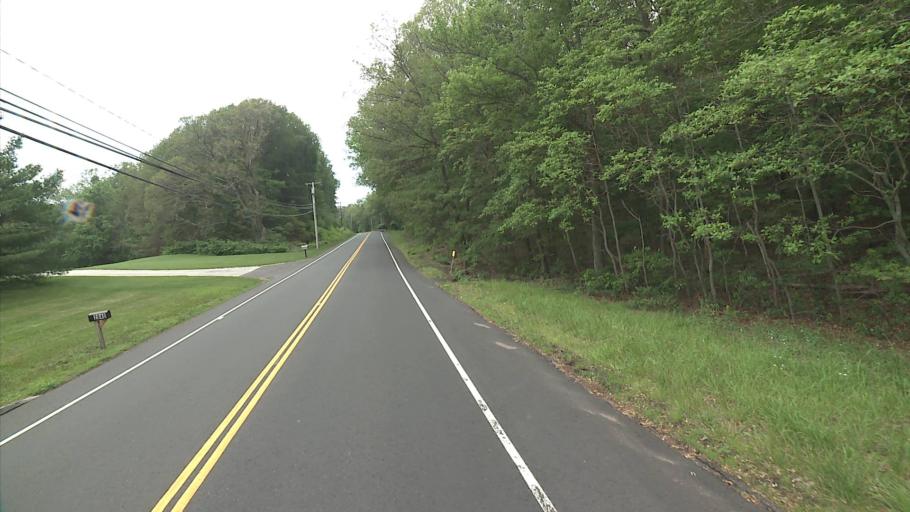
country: US
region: Connecticut
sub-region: Hartford County
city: Manchester
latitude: 41.7095
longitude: -72.4955
